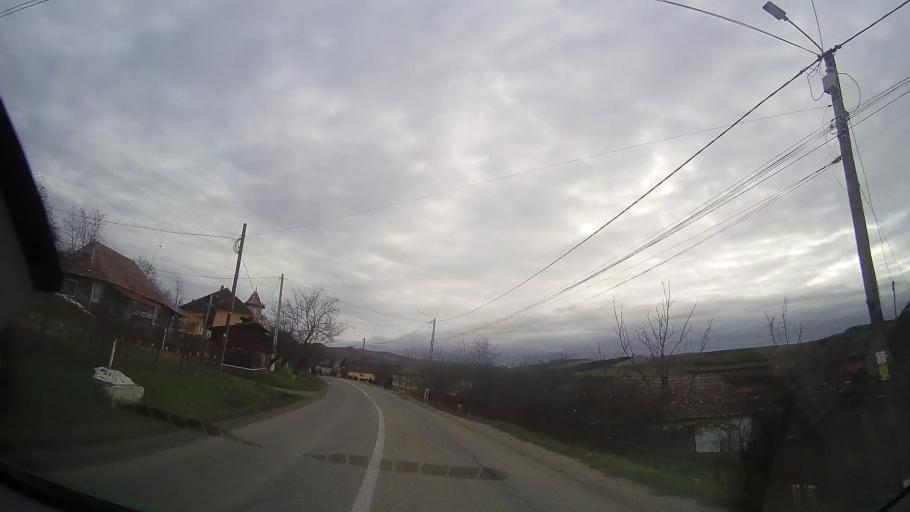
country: RO
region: Bistrita-Nasaud
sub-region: Comuna Budesti
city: Budesti
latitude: 46.8794
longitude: 24.2395
